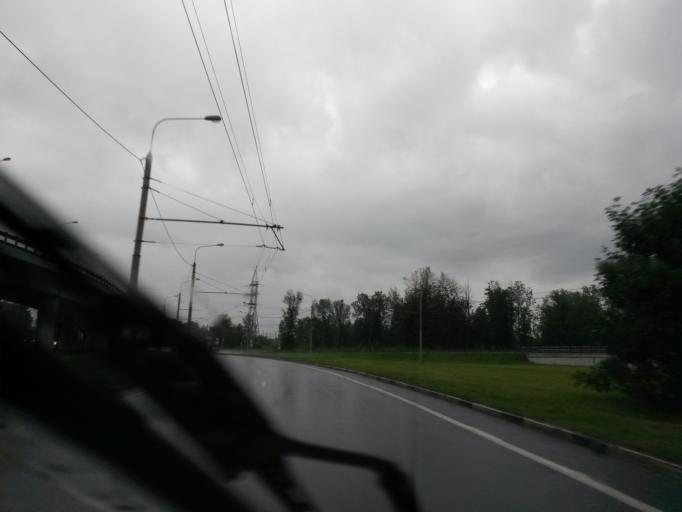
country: RU
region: Jaroslavl
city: Yaroslavl
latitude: 57.6684
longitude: 39.8401
